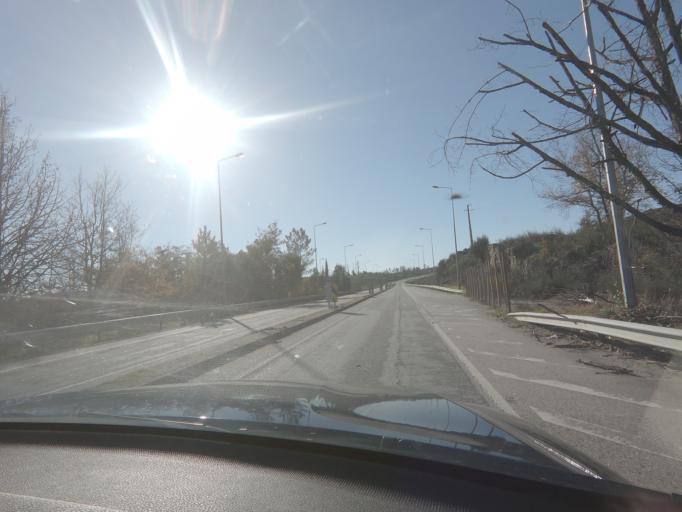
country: PT
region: Viseu
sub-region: Vouzela
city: Vouzela
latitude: 40.6511
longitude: -8.0407
